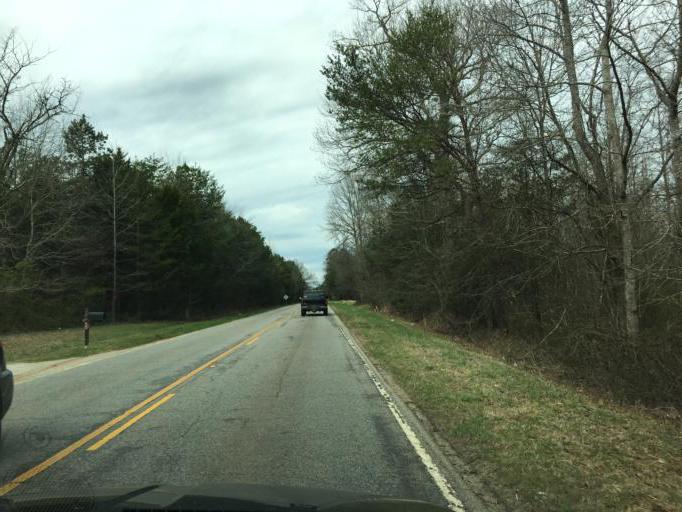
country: US
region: South Carolina
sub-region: Anderson County
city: Piedmont
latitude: 34.7013
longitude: -82.4311
